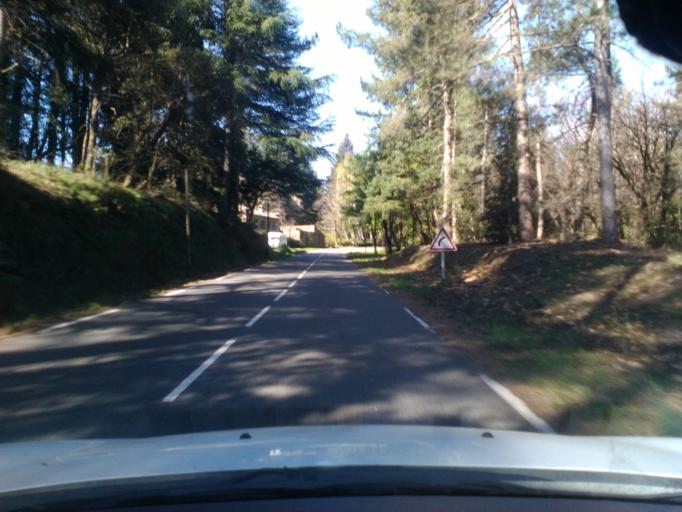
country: FR
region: Languedoc-Roussillon
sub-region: Departement du Gard
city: Saint-Jean-du-Gard
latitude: 44.1376
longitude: 3.8277
